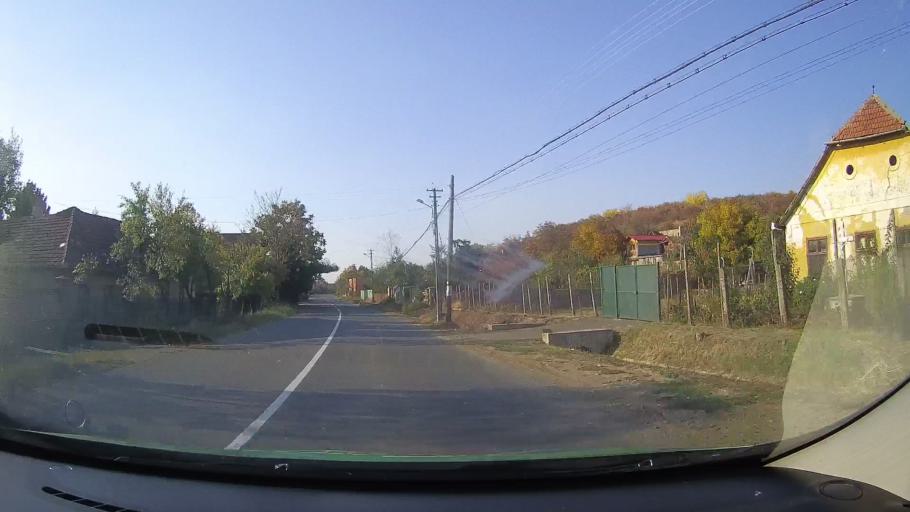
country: RO
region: Arad
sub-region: Comuna Ghioroc
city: Ghioroc
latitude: 46.1447
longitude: 21.5996
